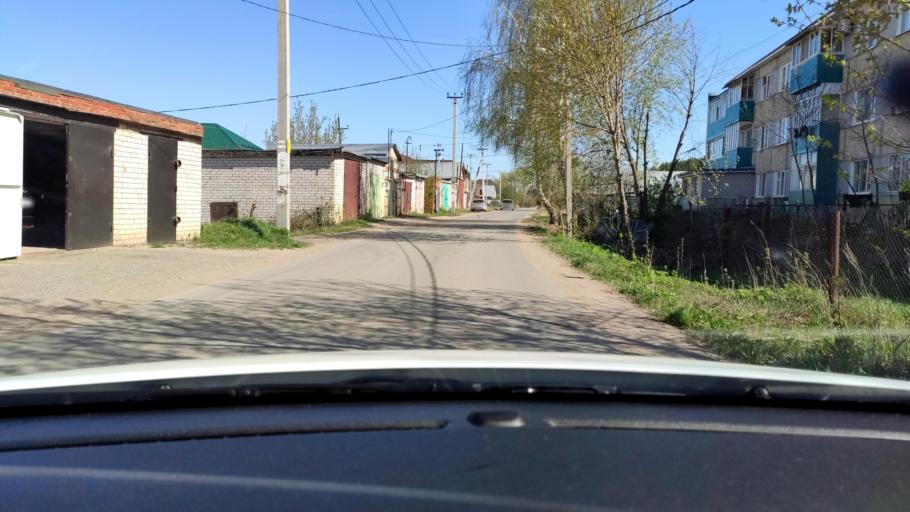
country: RU
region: Tatarstan
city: Vysokaya Gora
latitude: 55.8765
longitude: 49.2462
